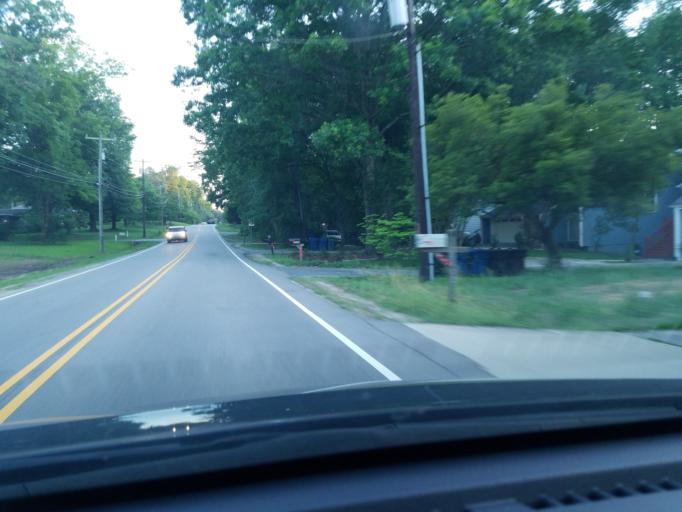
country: US
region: North Carolina
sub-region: Durham County
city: Durham
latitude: 35.9656
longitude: -78.9326
